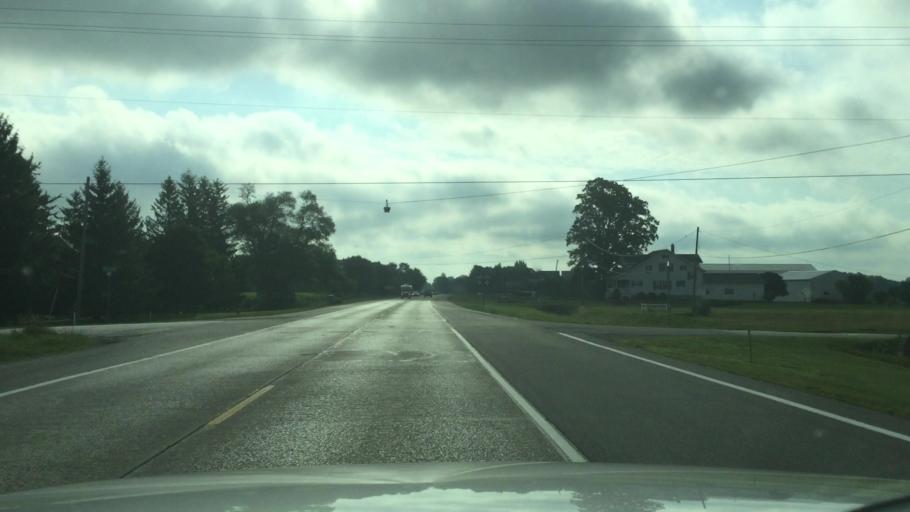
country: US
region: Michigan
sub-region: Saginaw County
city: Birch Run
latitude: 43.2502
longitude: -83.7551
